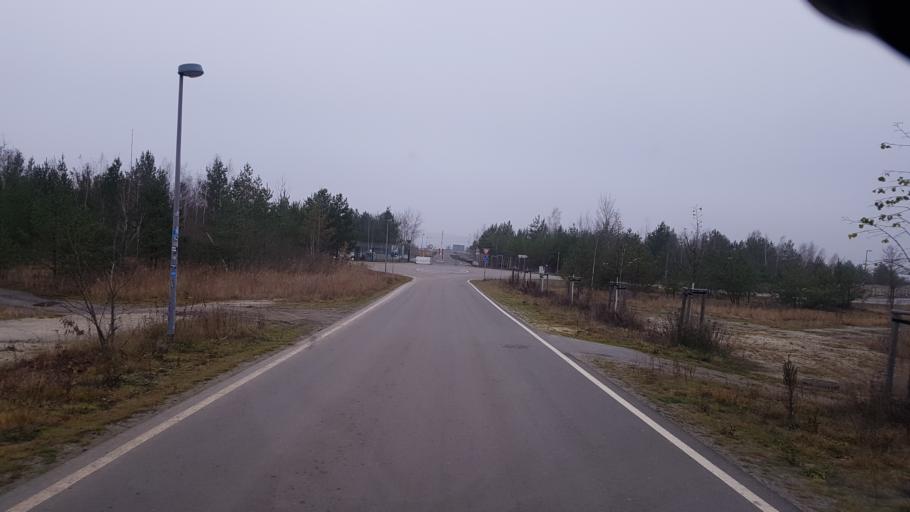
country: DE
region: Brandenburg
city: Sallgast
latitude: 51.5867
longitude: 13.7861
